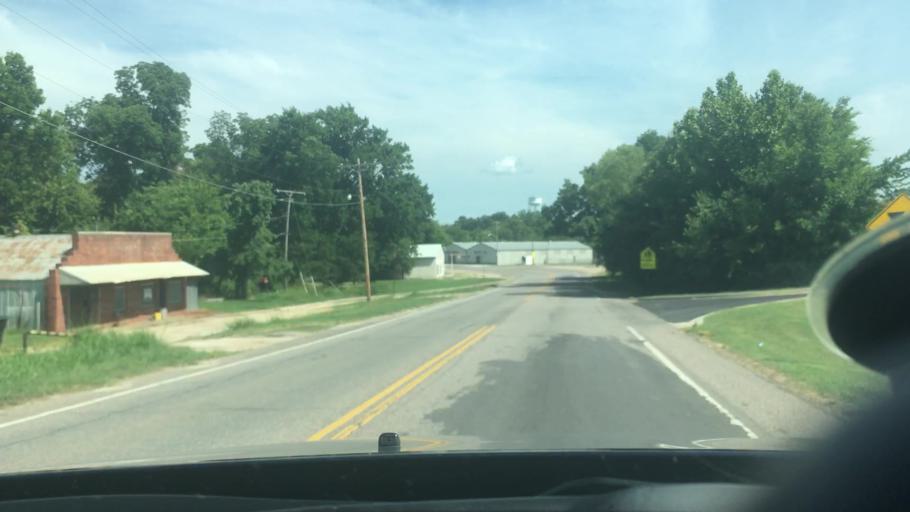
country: US
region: Oklahoma
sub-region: Seminole County
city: Seminole
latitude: 35.2262
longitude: -96.6807
